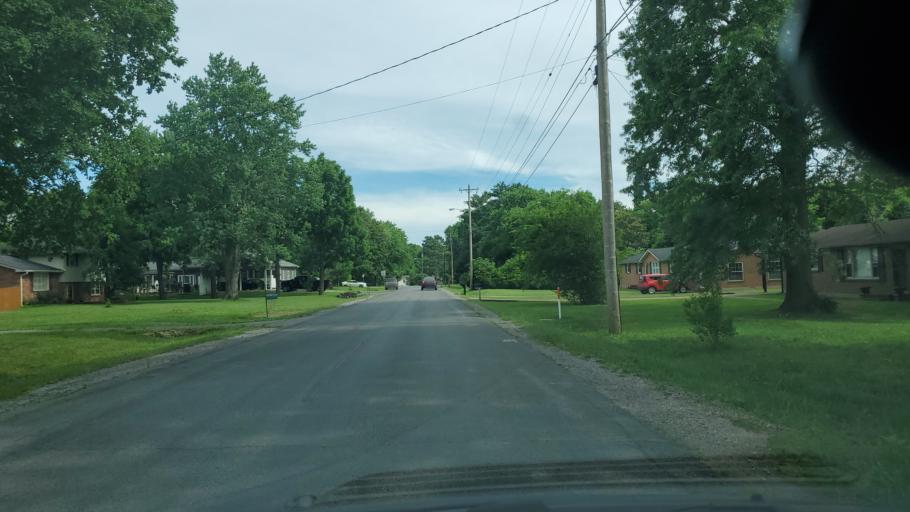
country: US
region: Tennessee
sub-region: Davidson County
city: Lakewood
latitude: 36.2048
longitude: -86.6885
